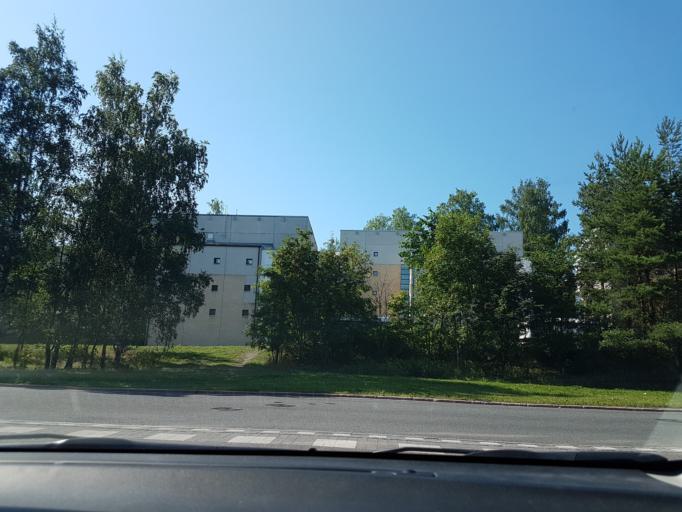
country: FI
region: Uusimaa
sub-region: Helsinki
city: Vantaa
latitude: 60.2542
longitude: 25.0191
